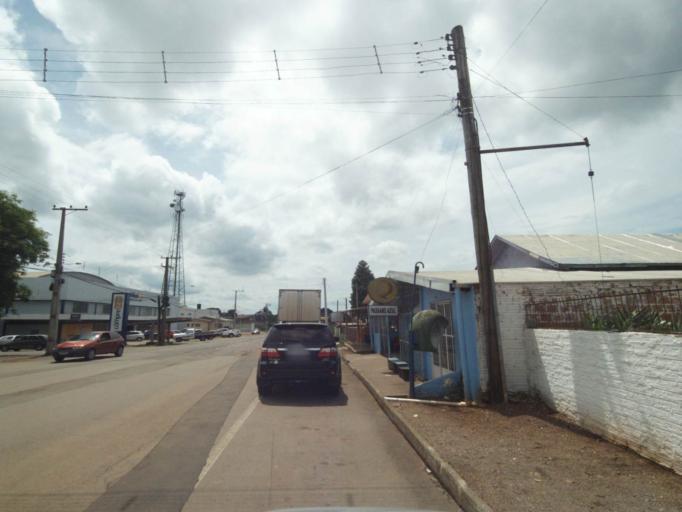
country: BR
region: Rio Grande do Sul
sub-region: Lagoa Vermelha
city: Lagoa Vermelha
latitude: -28.2201
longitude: -51.5141
